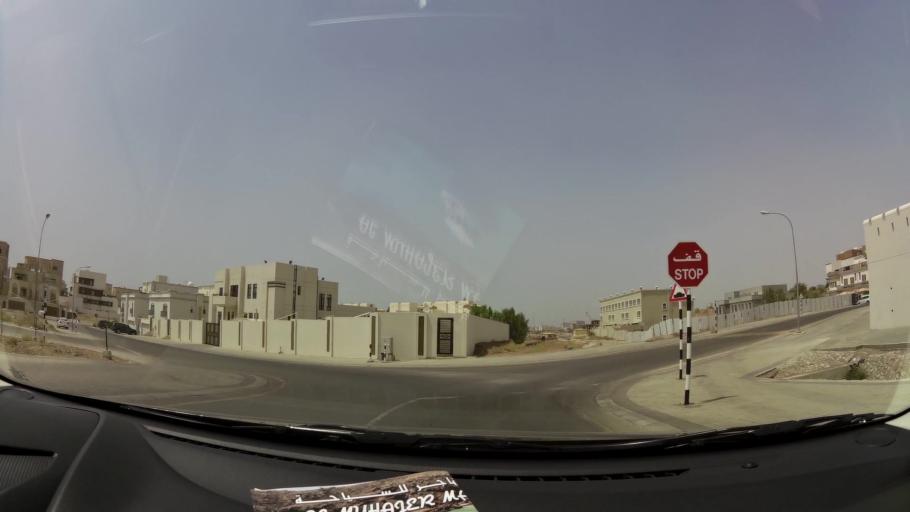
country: OM
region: Muhafazat Masqat
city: Bawshar
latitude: 23.5645
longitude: 58.3998
